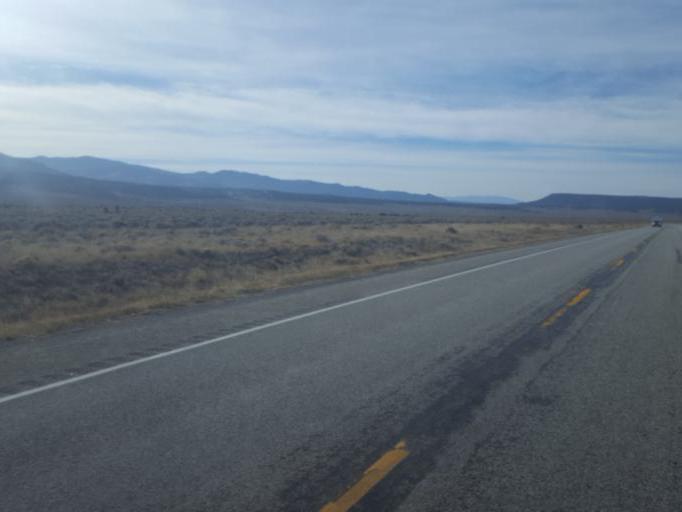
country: US
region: Colorado
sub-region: Costilla County
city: San Luis
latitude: 37.4682
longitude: -105.3526
